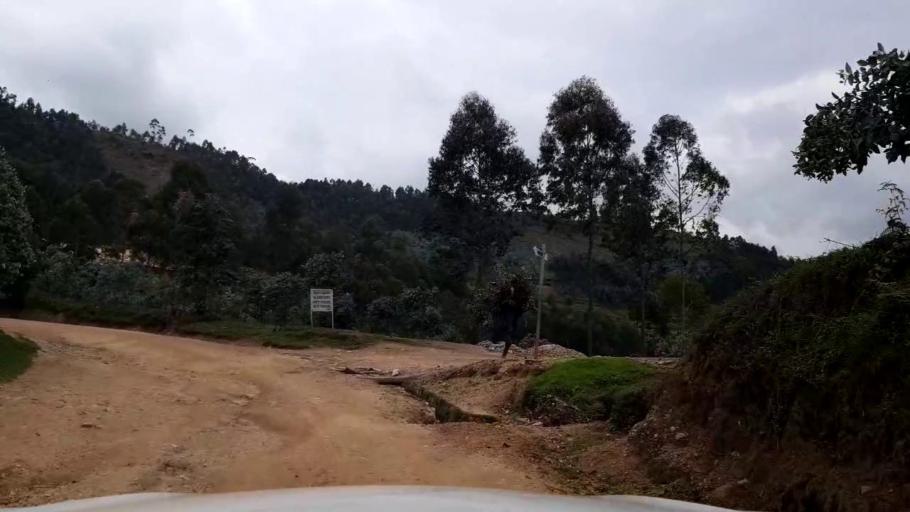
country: RW
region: Western Province
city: Kibuye
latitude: -1.9679
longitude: 29.3941
